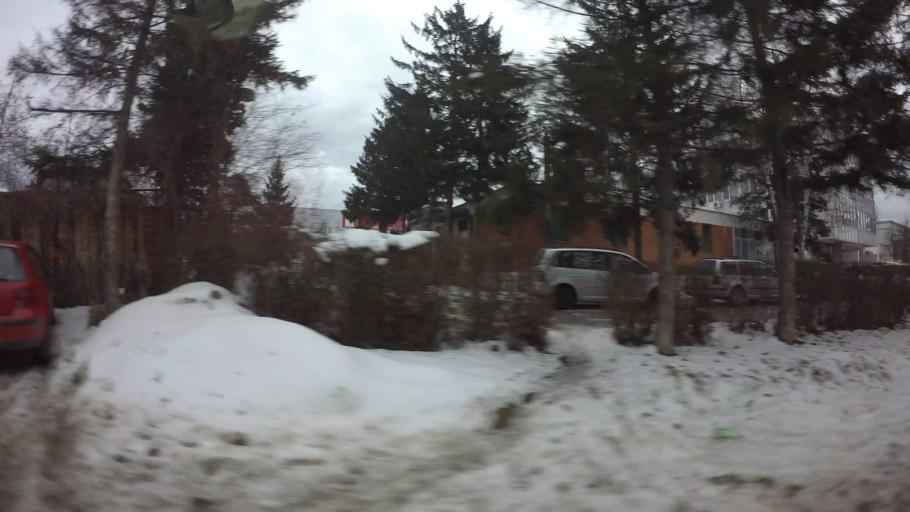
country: BA
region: Federation of Bosnia and Herzegovina
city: Vogosca
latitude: 43.8789
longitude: 18.3078
